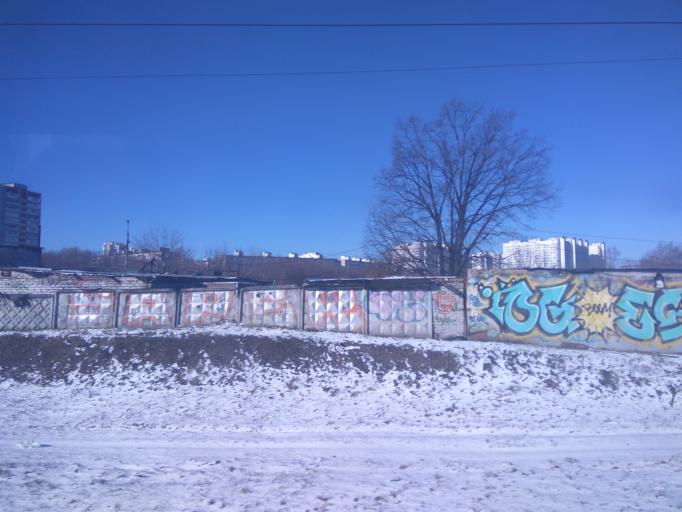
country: RU
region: Moscow
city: Tekstil'shchiki
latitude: 55.6935
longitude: 37.7317
